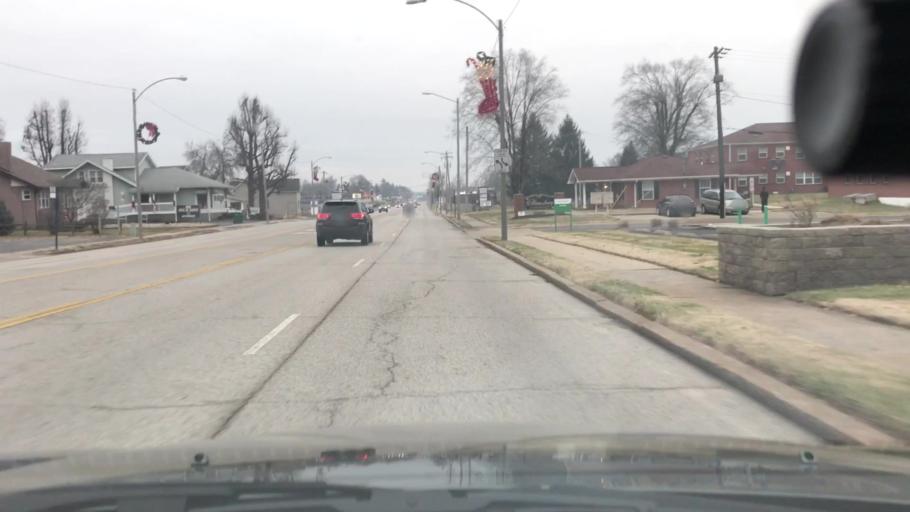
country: US
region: Illinois
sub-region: Saint Clair County
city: Swansea
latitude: 38.5561
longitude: -90.0424
